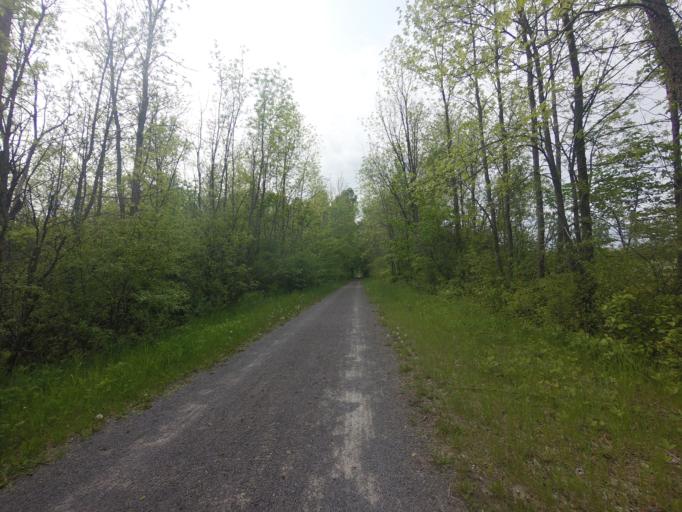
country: CA
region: Ontario
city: Kingston
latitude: 44.3396
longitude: -76.5964
